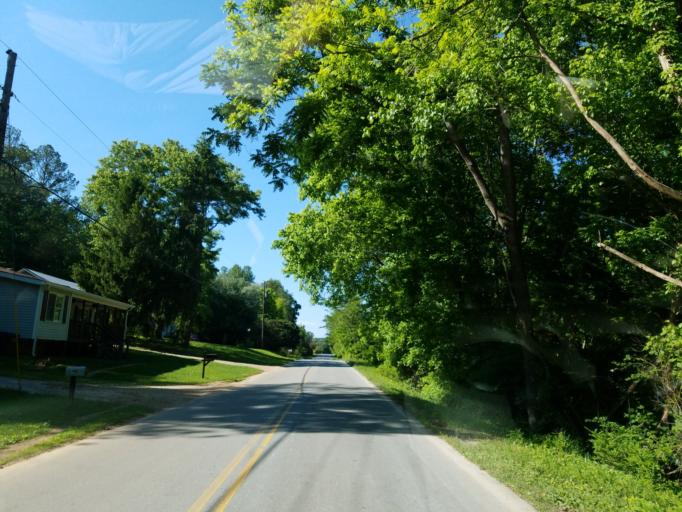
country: US
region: Georgia
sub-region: Pickens County
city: Jasper
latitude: 34.5602
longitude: -84.5116
